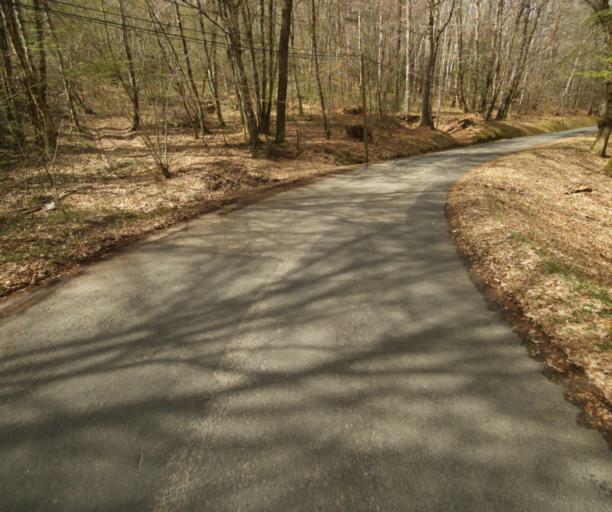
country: FR
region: Limousin
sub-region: Departement de la Correze
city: Laguenne
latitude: 45.2377
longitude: 1.8666
